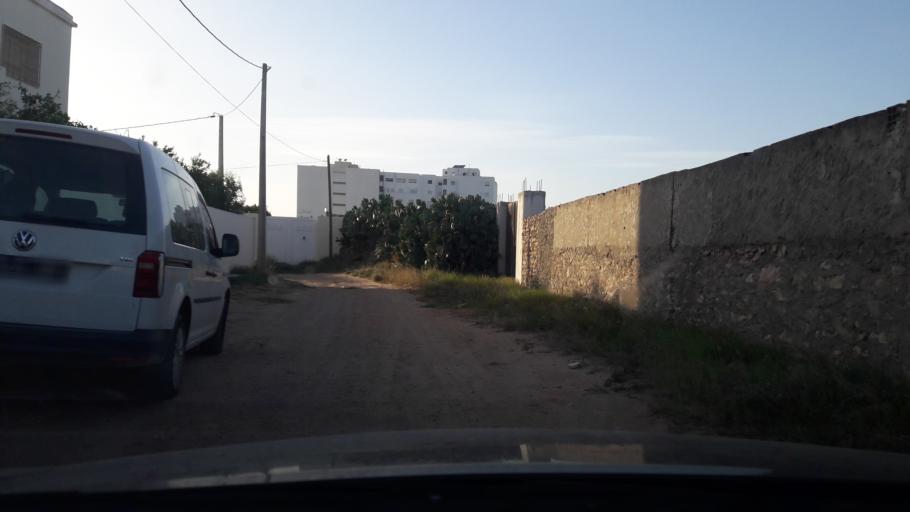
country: TN
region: Safaqis
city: Al Qarmadah
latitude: 34.7964
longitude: 10.7567
